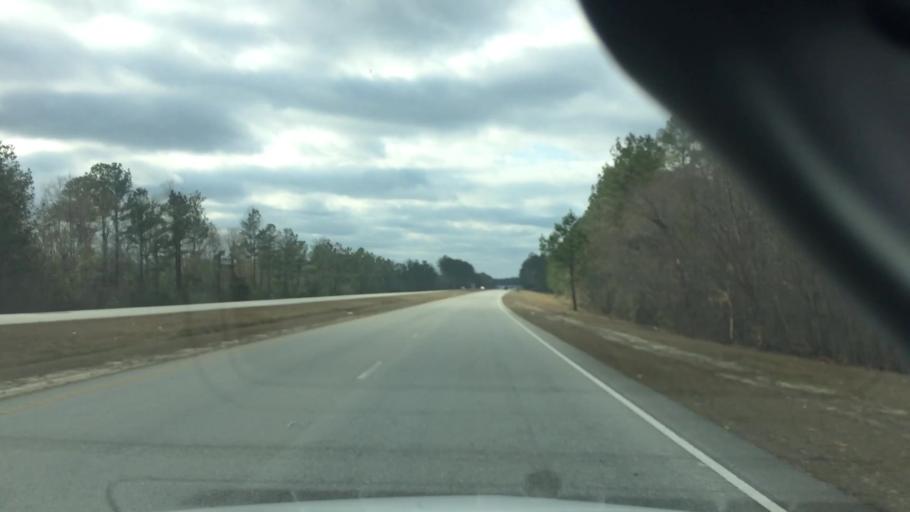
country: US
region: North Carolina
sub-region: Brunswick County
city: Bolivia
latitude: 34.0675
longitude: -78.1807
